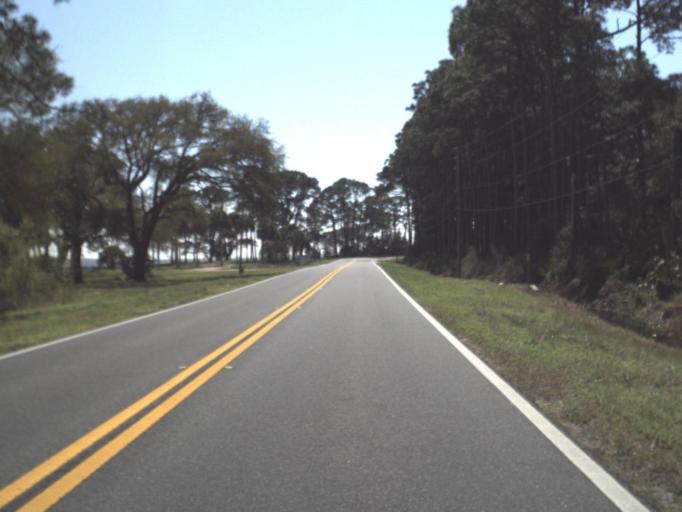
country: US
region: Florida
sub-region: Franklin County
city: Carrabelle
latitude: 29.8553
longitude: -84.6349
